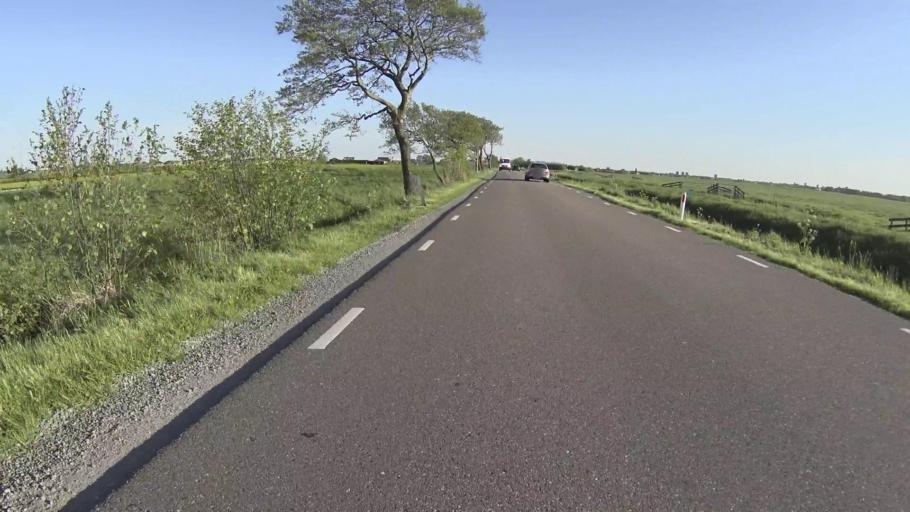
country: NL
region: South Holland
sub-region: Gemeente Rijnwoude
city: Benthuizen
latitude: 52.1109
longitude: 4.5359
